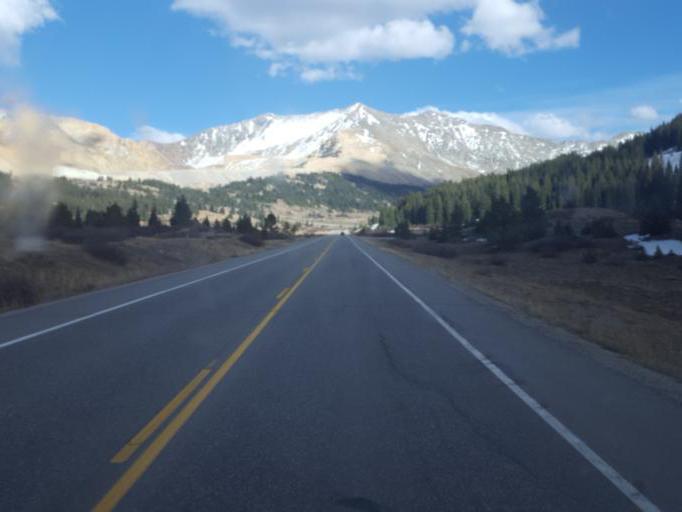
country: US
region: Colorado
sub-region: Lake County
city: Leadville
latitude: 39.3604
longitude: -106.2008
